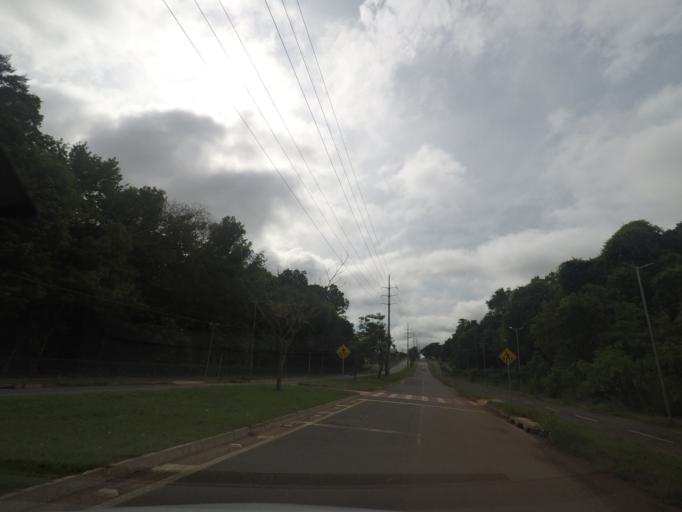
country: BR
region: Goias
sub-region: Goiania
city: Goiania
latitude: -16.7385
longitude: -49.3201
